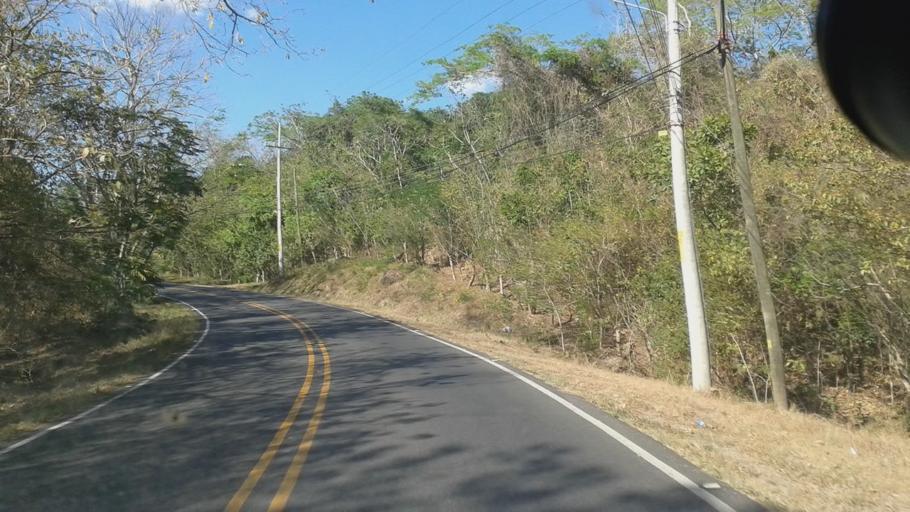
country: CR
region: Guanacaste
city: Samara
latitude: 9.9295
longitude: -85.5169
